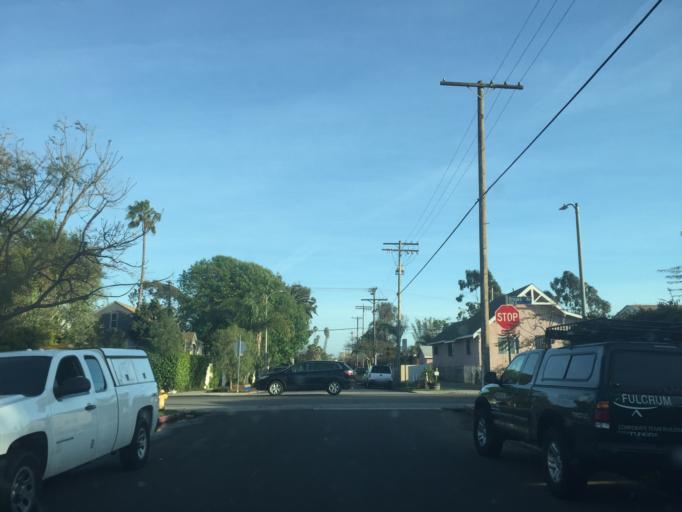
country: US
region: California
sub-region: Los Angeles County
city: Marina del Rey
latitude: 33.9957
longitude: -118.4691
